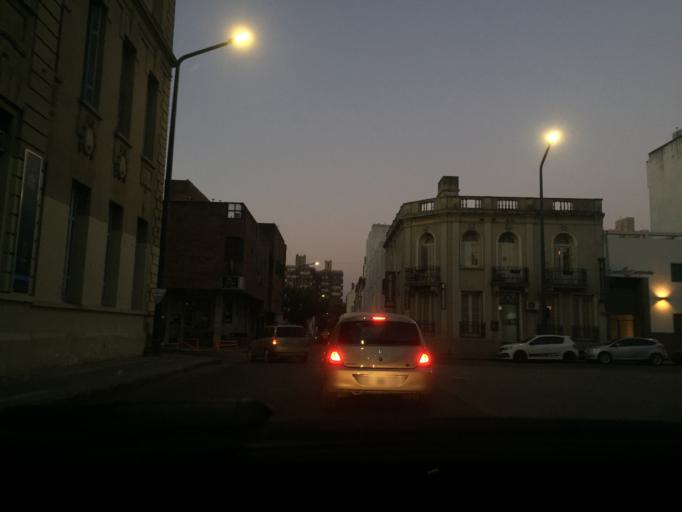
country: AR
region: Cordoba
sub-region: Departamento de Capital
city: Cordoba
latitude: -31.4089
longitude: -64.1964
